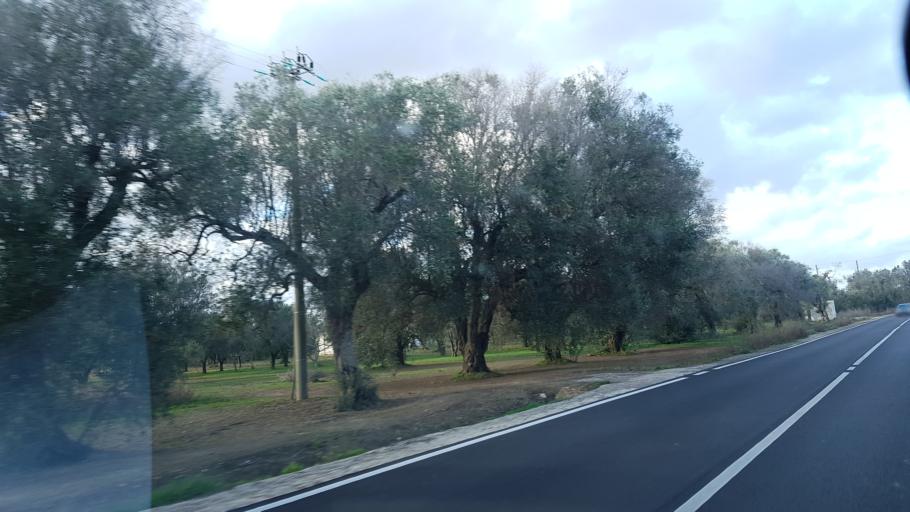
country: IT
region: Apulia
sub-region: Provincia di Brindisi
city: San Pietro Vernotico
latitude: 40.5061
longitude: 18.0080
